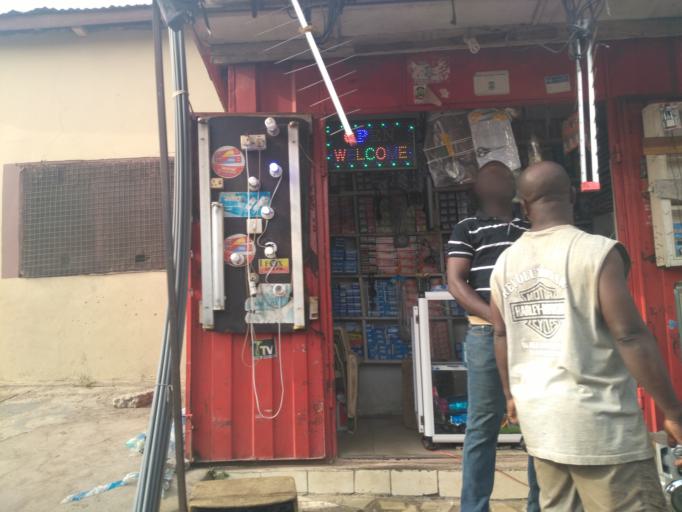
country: GH
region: Ashanti
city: Kumasi
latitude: 6.6857
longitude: -1.6103
